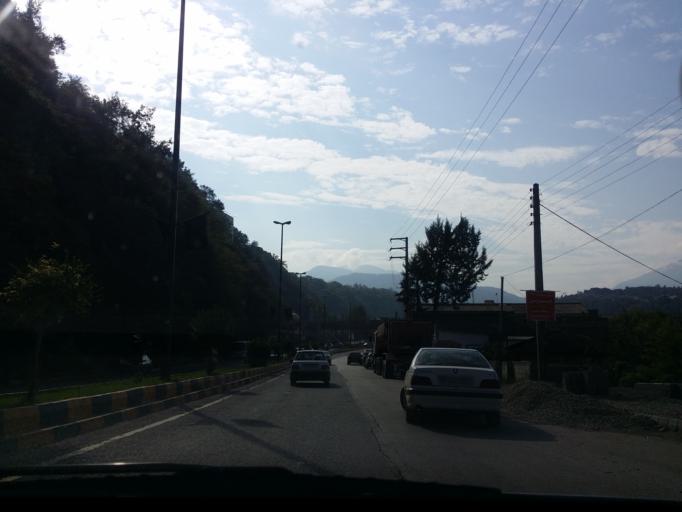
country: IR
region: Mazandaran
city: Chalus
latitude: 36.6482
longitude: 51.4140
